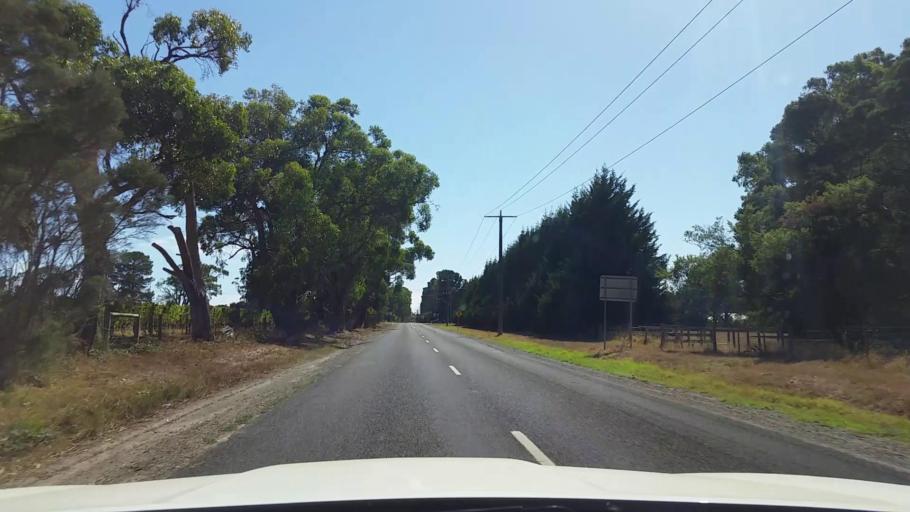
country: AU
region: Victoria
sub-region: Mornington Peninsula
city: Balnarring
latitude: -38.3409
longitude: 145.1457
